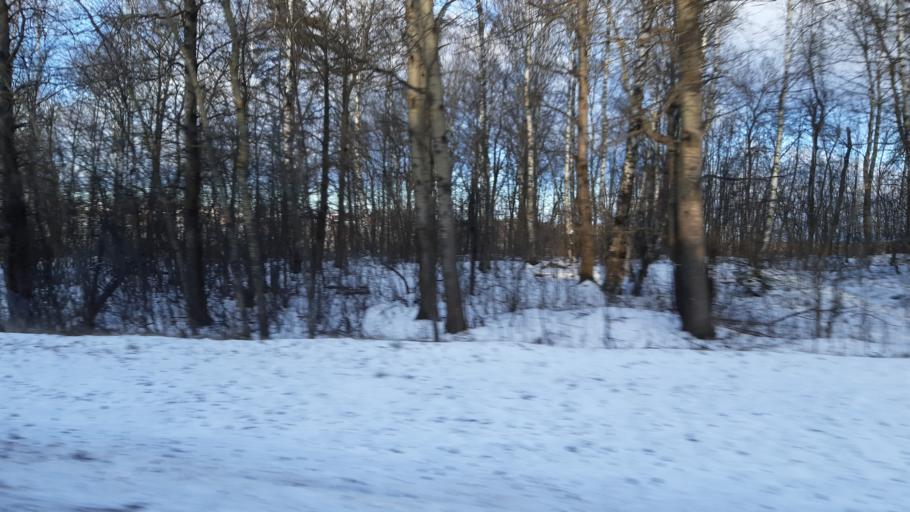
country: RU
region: Moskovskaya
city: Svatkovo
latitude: 56.3087
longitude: 38.3245
